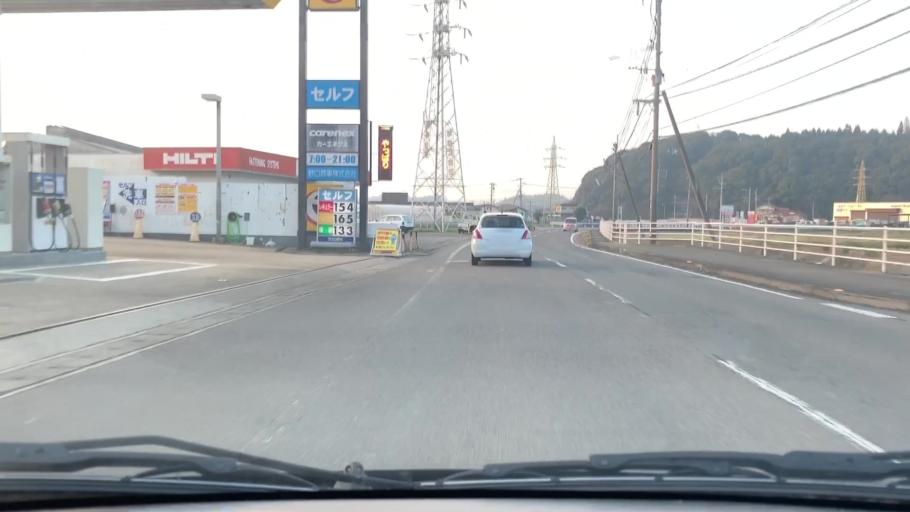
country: JP
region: Saga Prefecture
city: Imaricho-ko
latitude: 33.2695
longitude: 129.8966
